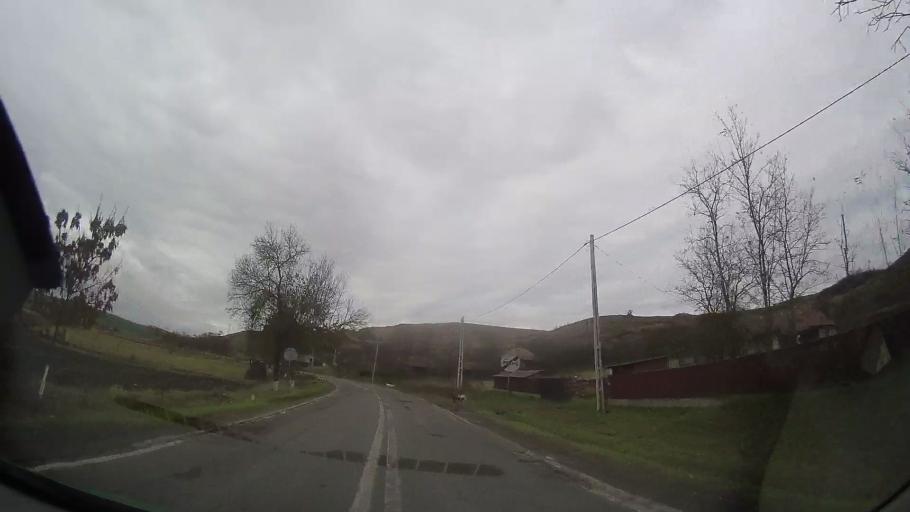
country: RO
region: Mures
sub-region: Comuna Craesti
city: Craiesti
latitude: 46.7604
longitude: 24.3956
